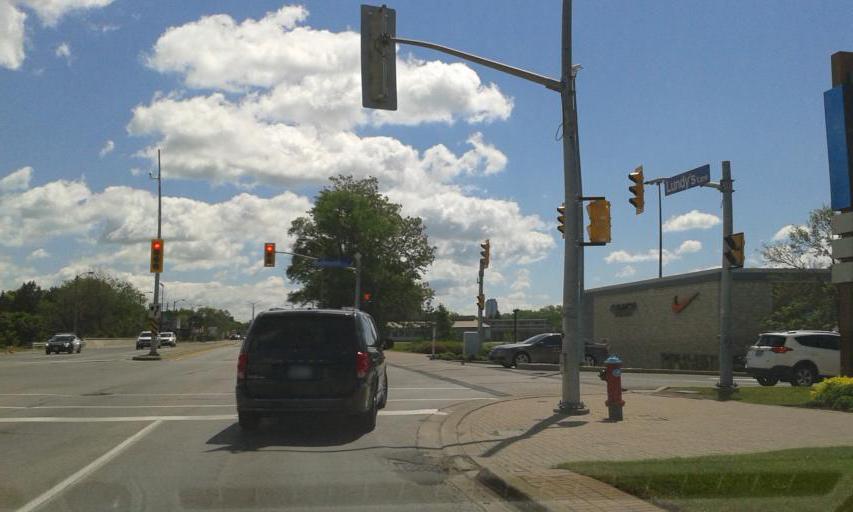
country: CA
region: Ontario
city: Niagara Falls
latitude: 43.0890
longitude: -79.1205
